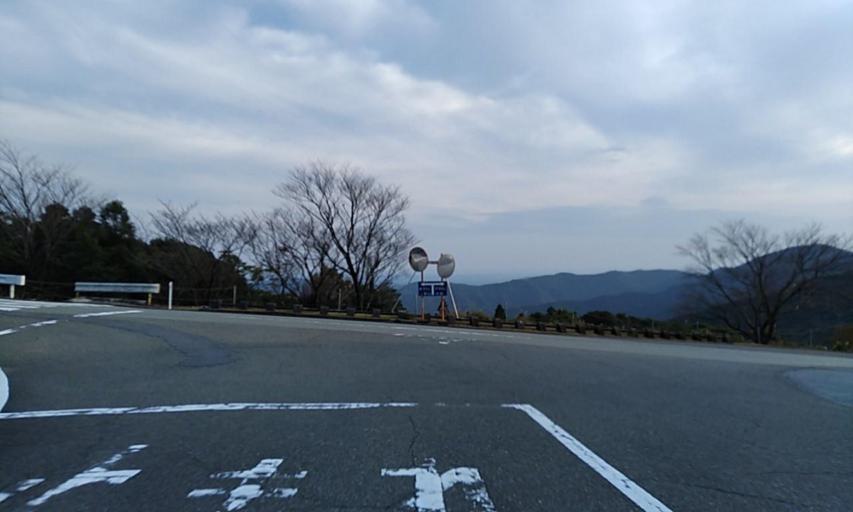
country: JP
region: Mie
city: Toba
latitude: 34.4591
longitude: 136.7892
